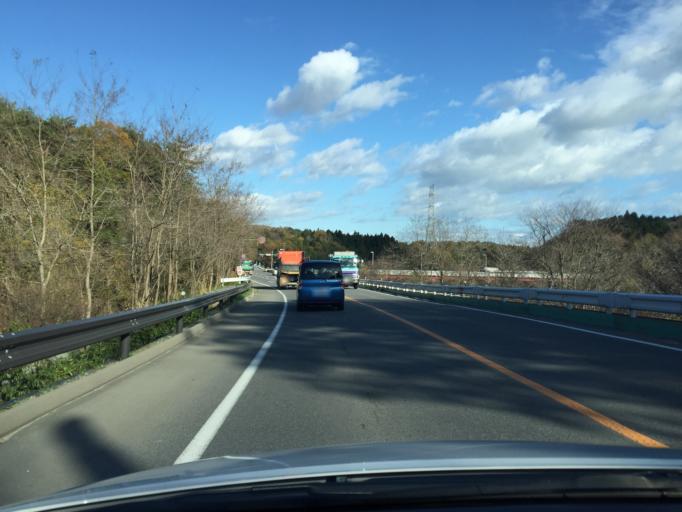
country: JP
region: Fukushima
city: Namie
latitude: 37.3111
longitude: 141.0007
